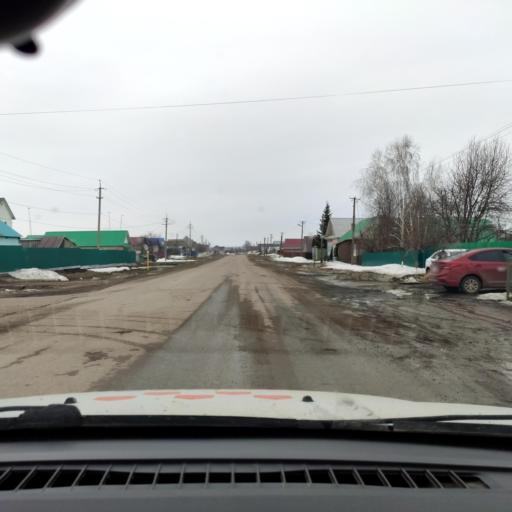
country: RU
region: Bashkortostan
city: Kushnarenkovo
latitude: 55.0804
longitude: 55.3897
